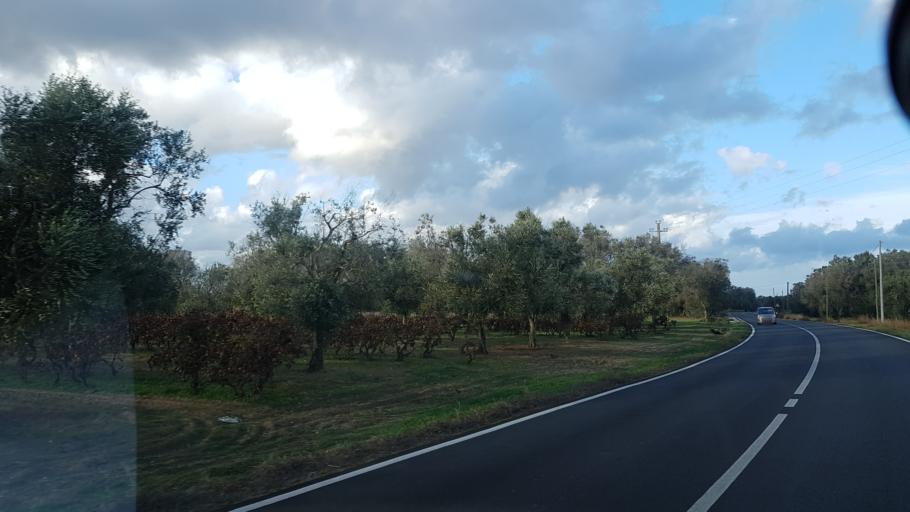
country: IT
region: Apulia
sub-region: Provincia di Brindisi
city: San Pietro Vernotico
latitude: 40.5050
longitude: 18.0077
